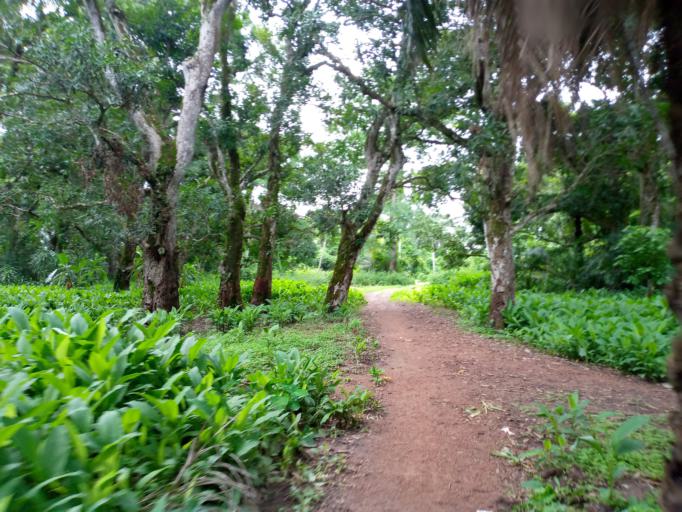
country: SL
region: Northern Province
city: Mange
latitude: 8.9798
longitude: -12.7418
